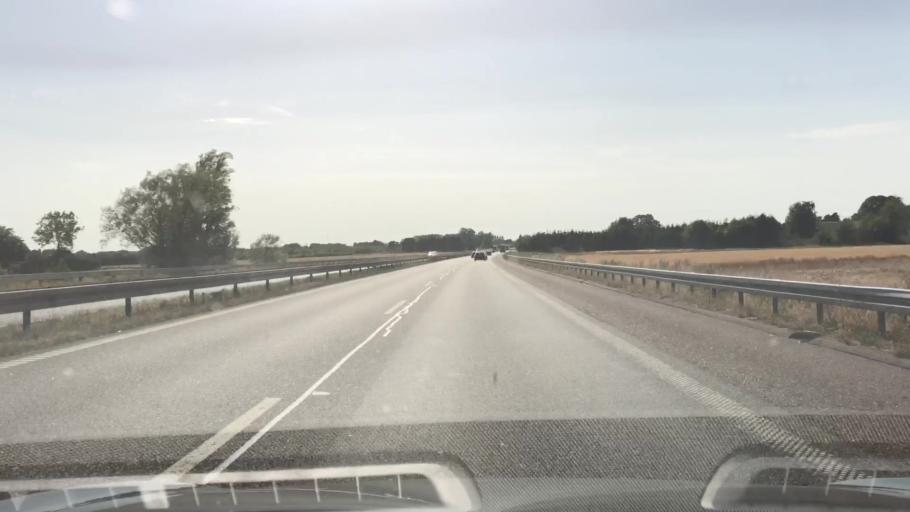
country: DK
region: Zealand
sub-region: Ringsted Kommune
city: Ringsted
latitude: 55.4510
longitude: 11.7009
